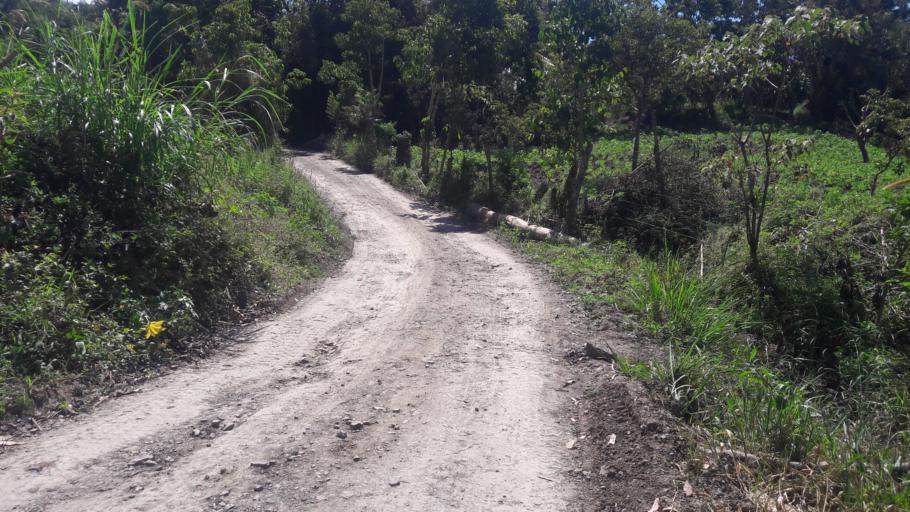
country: CO
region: Cundinamarca
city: Tenza
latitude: 5.0809
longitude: -73.4103
